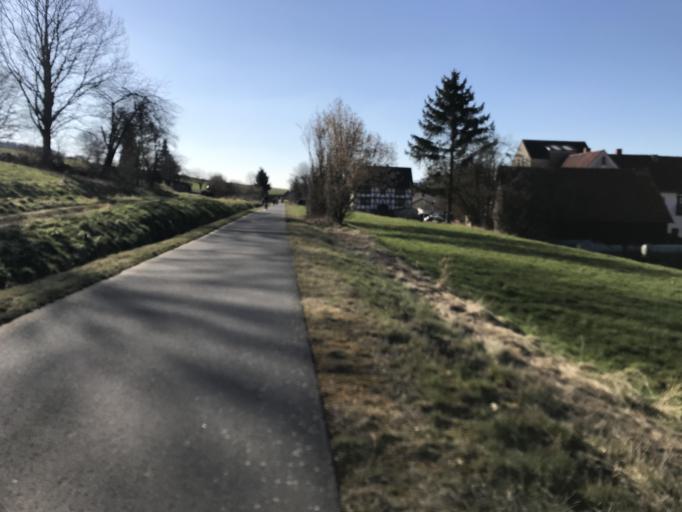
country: DE
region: Hesse
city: Neukirchen
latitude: 50.8748
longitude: 9.3126
